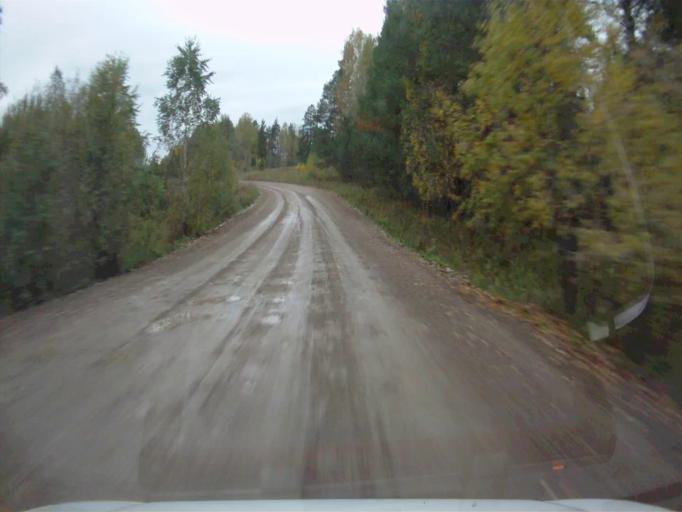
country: RU
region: Chelyabinsk
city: Nyazepetrovsk
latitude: 56.0908
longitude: 59.4132
